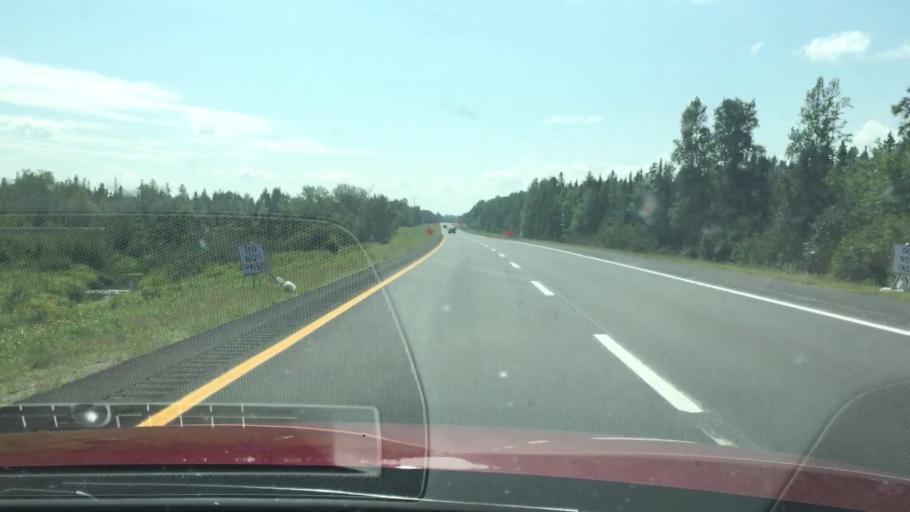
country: US
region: Maine
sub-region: Penobscot County
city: Patten
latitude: 45.8845
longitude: -68.4080
